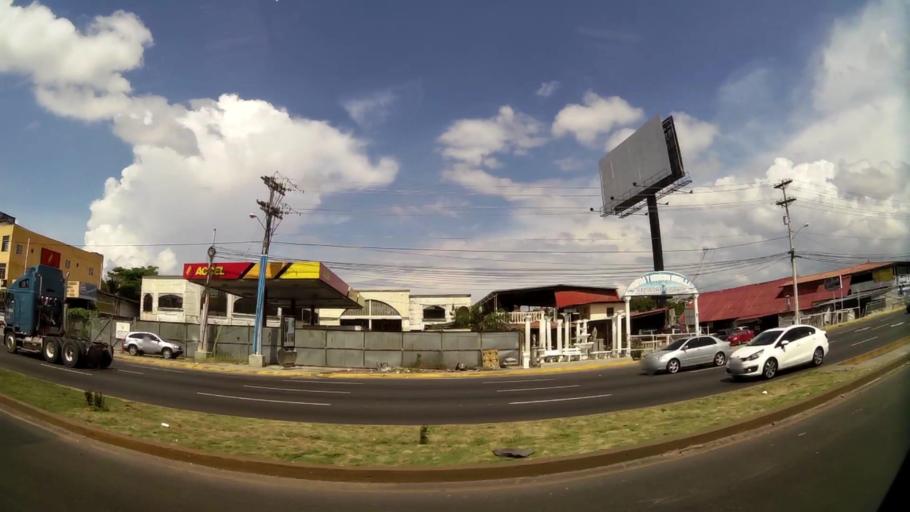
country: PA
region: Panama
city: San Miguelito
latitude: 9.0349
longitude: -79.4851
